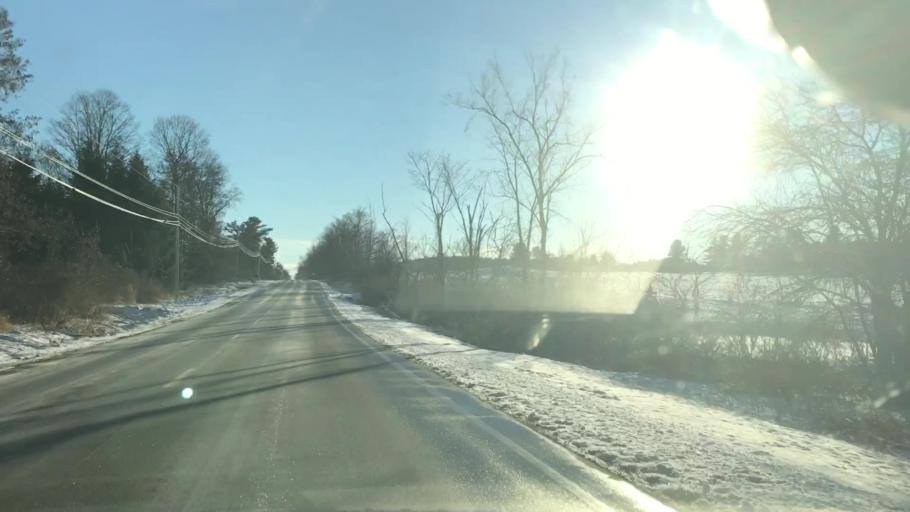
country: US
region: New Hampshire
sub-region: Grafton County
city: Haverhill
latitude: 44.0011
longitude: -72.0738
